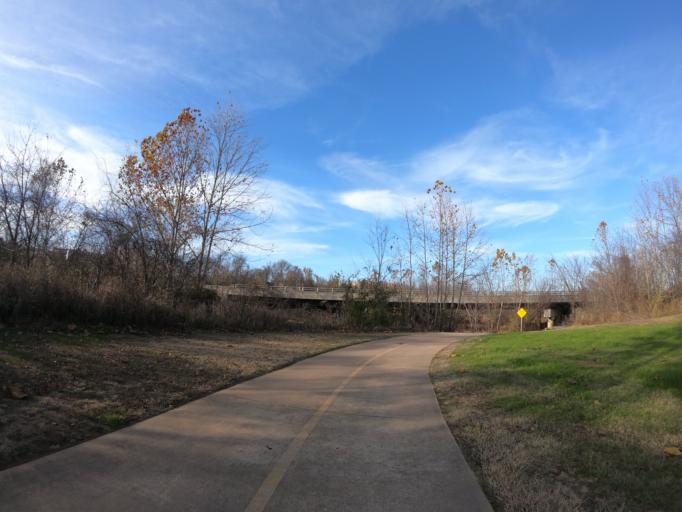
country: US
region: Arkansas
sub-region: Benton County
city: Cave Springs
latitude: 36.3042
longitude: -94.1806
